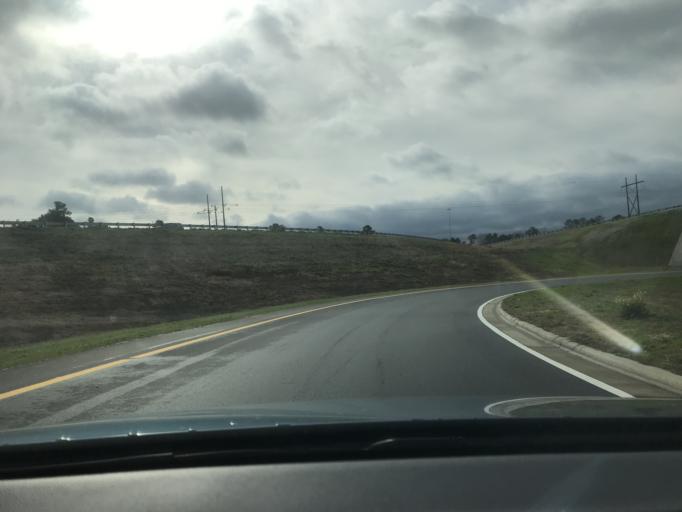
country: US
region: North Carolina
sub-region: Cumberland County
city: Fort Bragg
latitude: 35.1107
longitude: -78.9724
